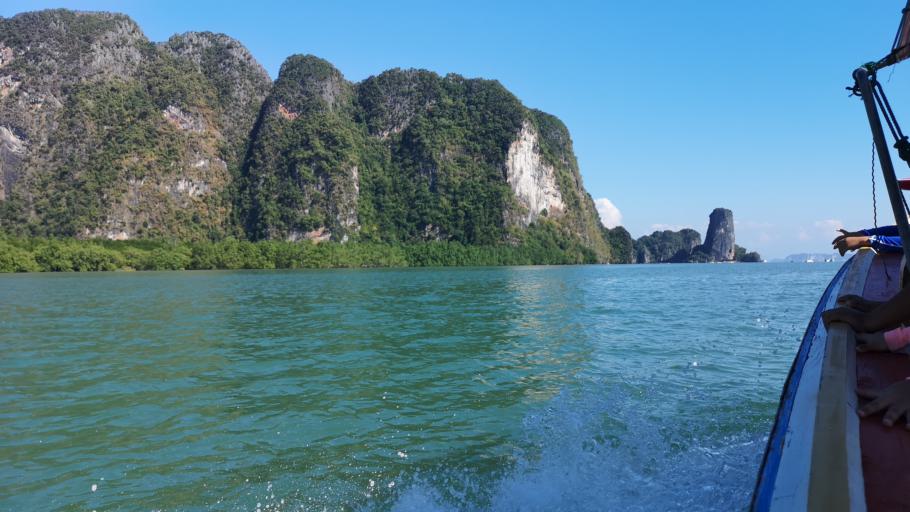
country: TH
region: Phangnga
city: Takua Thung
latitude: 8.2803
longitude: 98.4865
